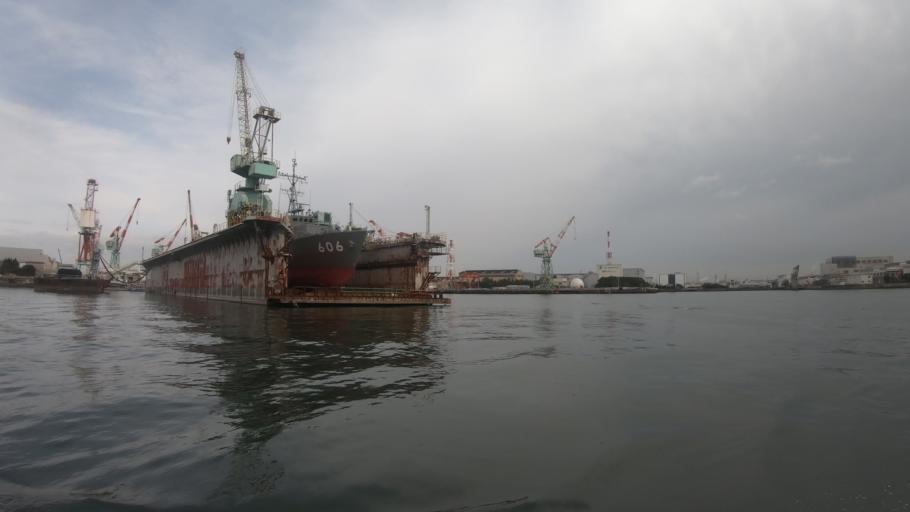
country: JP
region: Kanagawa
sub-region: Kawasaki-shi
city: Kawasaki
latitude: 35.4876
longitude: 139.6910
